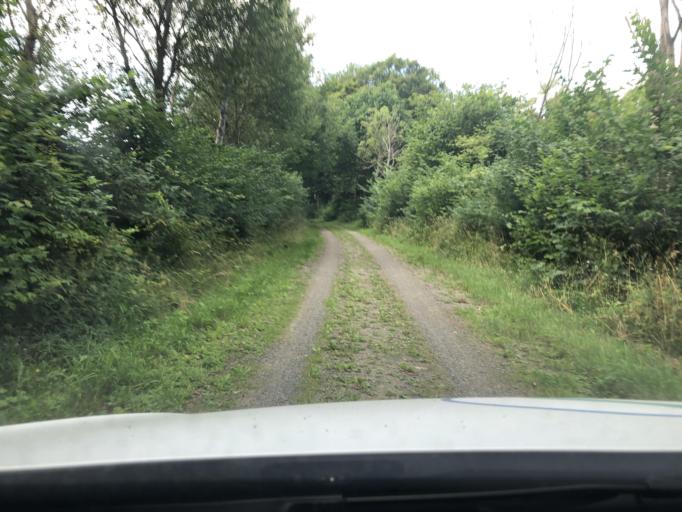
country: SE
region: Skane
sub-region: Kristianstads Kommun
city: Degeberga
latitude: 55.7849
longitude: 14.1728
